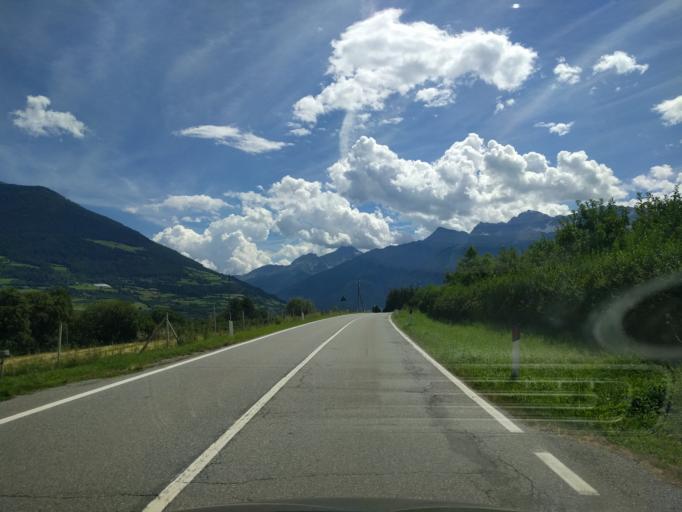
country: IT
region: Trentino-Alto Adige
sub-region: Bolzano
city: Glorenza
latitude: 46.6684
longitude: 10.5531
